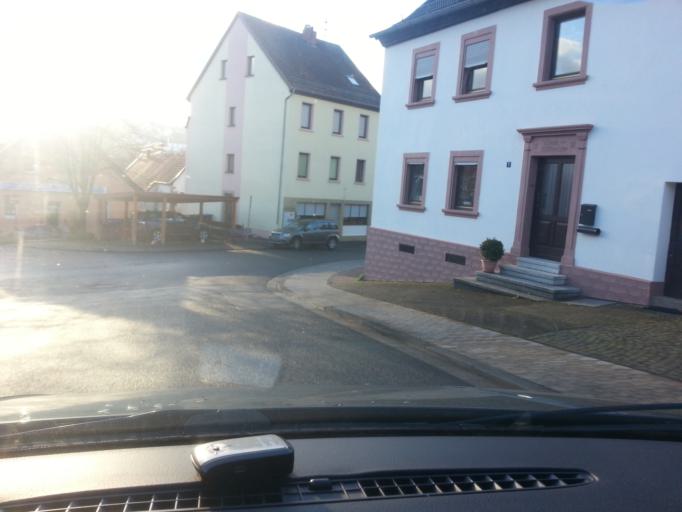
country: DE
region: Saarland
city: Ottweiler
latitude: 49.4334
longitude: 7.1615
